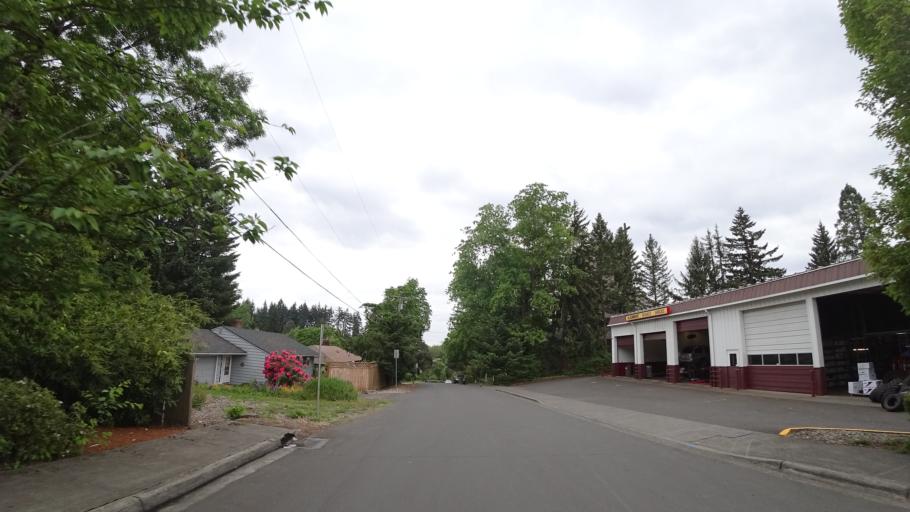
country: US
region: Oregon
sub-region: Washington County
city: West Slope
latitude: 45.4921
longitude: -122.7826
